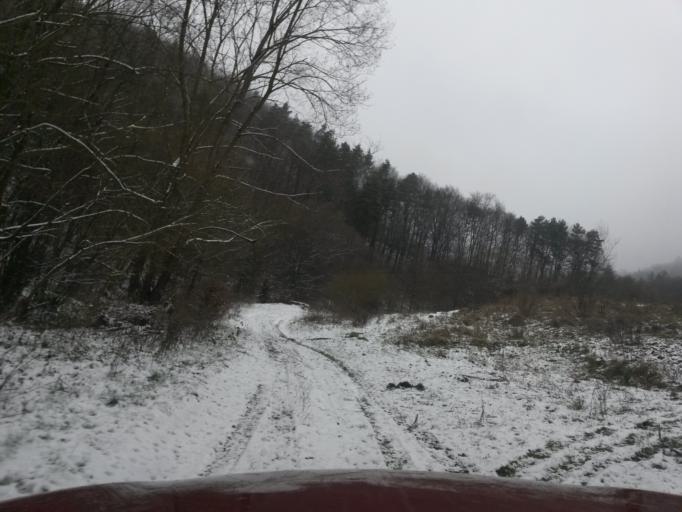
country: SK
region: Presovsky
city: Sabinov
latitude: 48.9704
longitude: 21.0888
